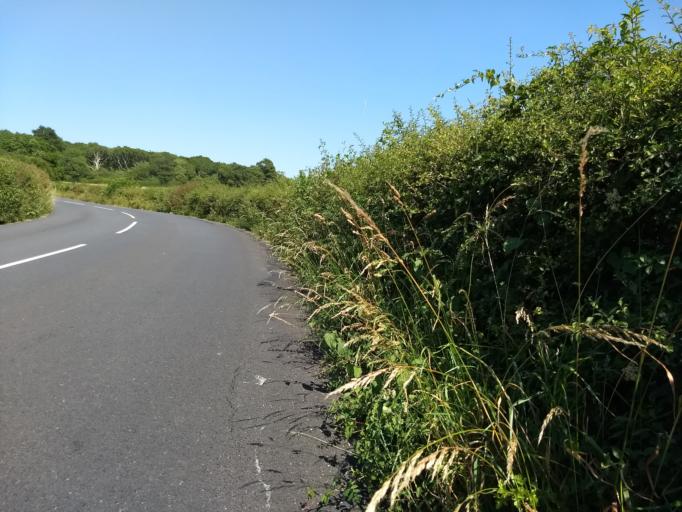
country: GB
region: England
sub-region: Isle of Wight
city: Shalfleet
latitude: 50.7212
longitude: -1.3641
